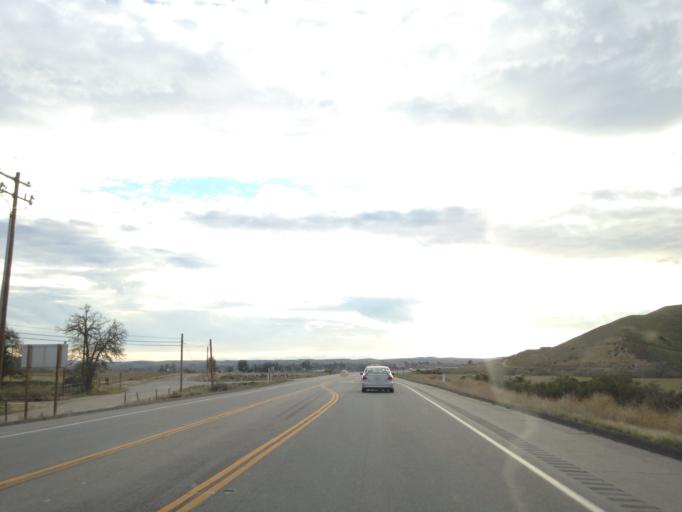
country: US
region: California
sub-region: San Luis Obispo County
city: Shandon
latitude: 35.6672
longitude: -120.3586
